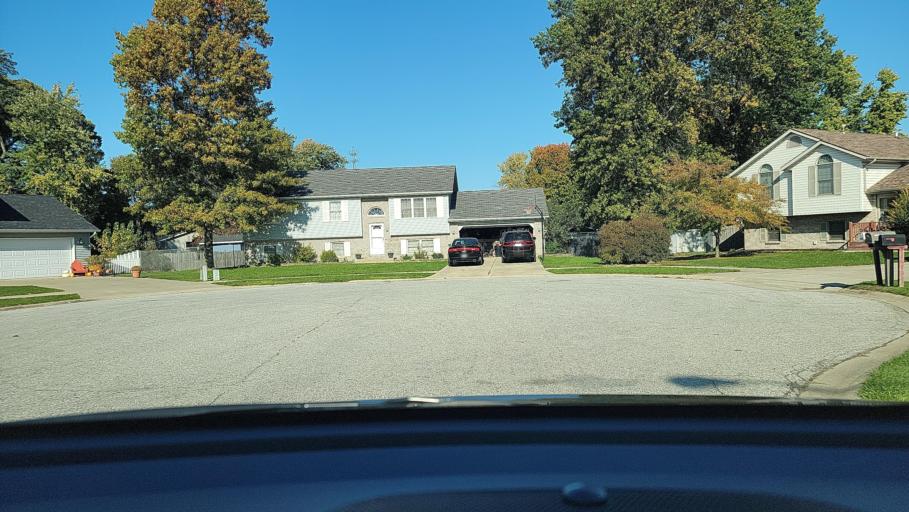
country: US
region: Indiana
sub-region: Porter County
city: Portage
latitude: 41.5809
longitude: -87.1632
